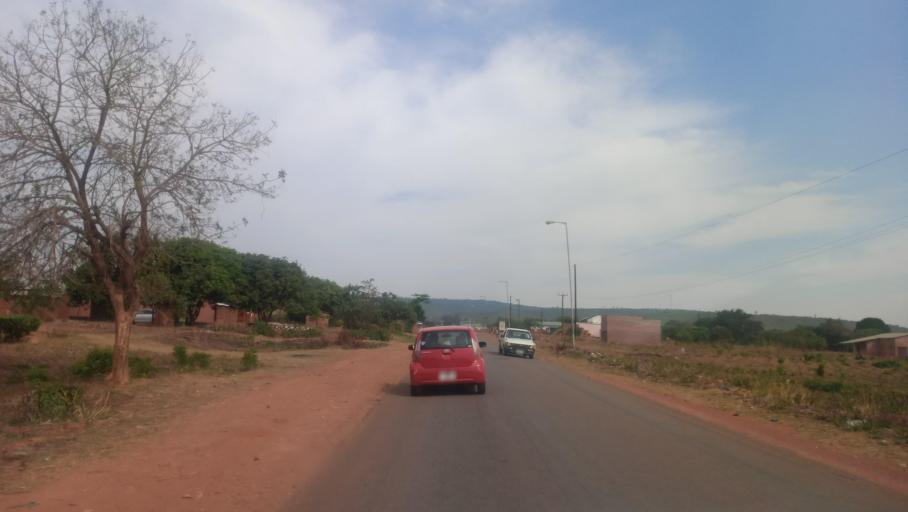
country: ZM
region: Northern
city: Mpika
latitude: -11.8407
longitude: 31.4377
